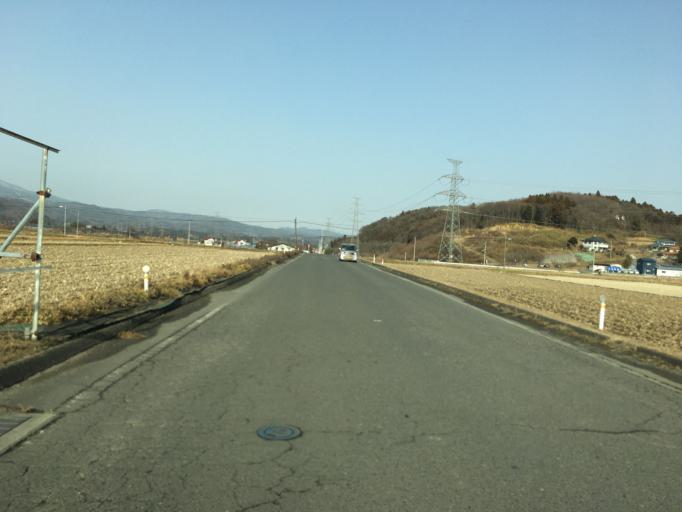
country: JP
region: Fukushima
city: Motomiya
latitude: 37.5431
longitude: 140.3946
